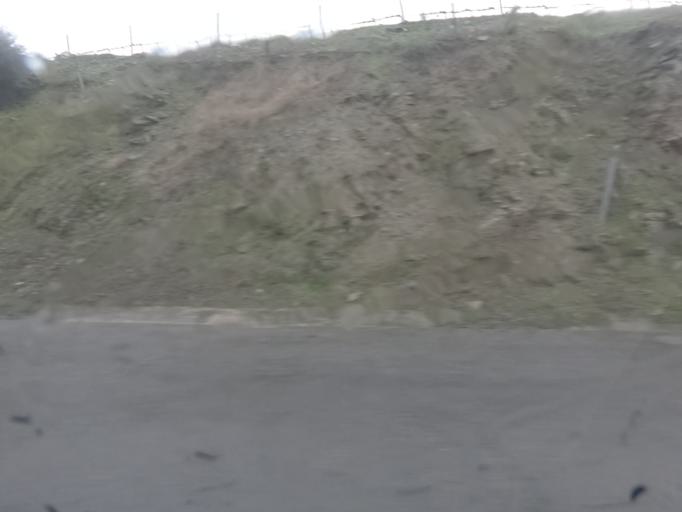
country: PT
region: Vila Real
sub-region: Peso da Regua
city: Peso da Regua
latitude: 41.1692
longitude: -7.7578
